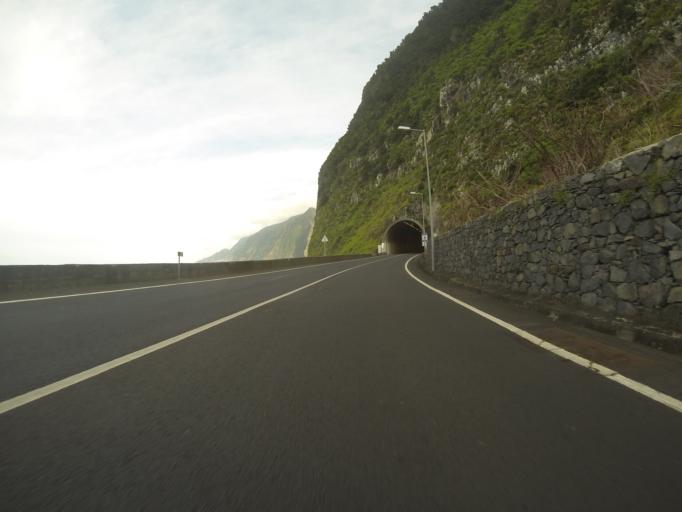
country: PT
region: Madeira
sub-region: Sao Vicente
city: Sao Vicente
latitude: 32.8134
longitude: -17.0707
